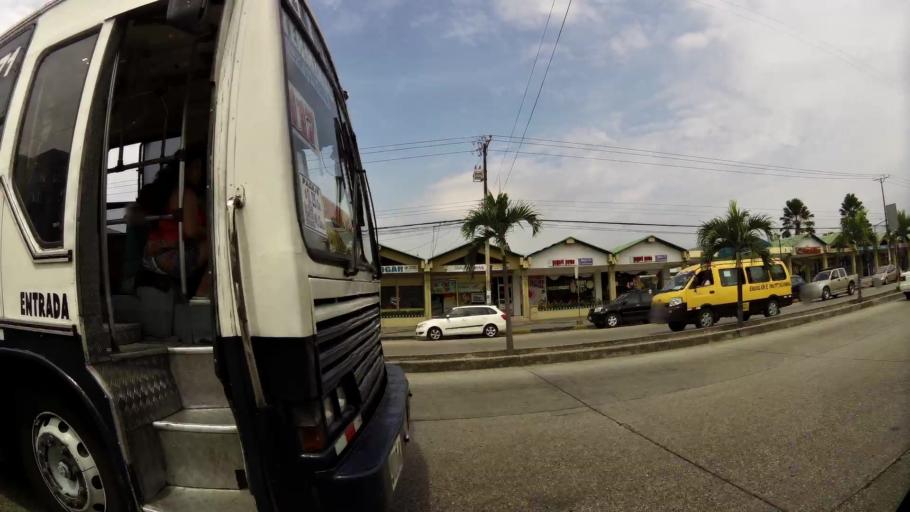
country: EC
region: Guayas
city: Eloy Alfaro
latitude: -2.1440
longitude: -79.8939
